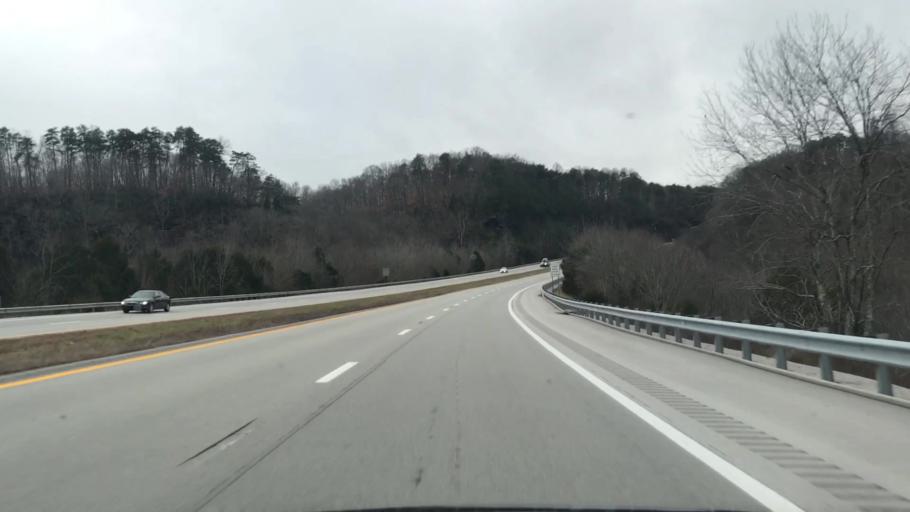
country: US
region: Kentucky
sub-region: Russell County
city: Russell Springs
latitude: 37.0884
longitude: -84.8864
